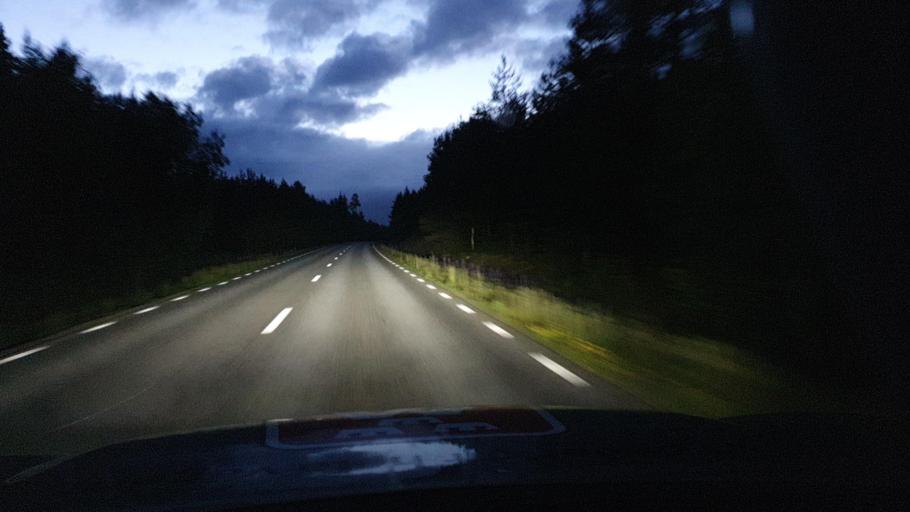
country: SE
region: OErebro
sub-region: Karlskoga Kommun
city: Karlskoga
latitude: 59.4960
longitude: 14.4938
